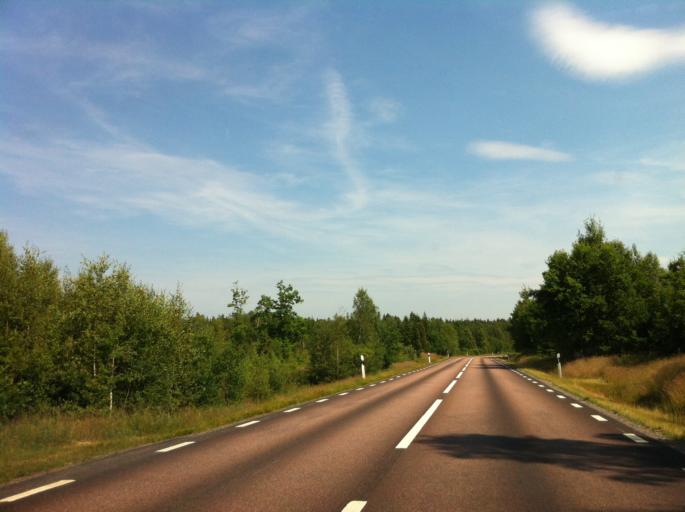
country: SE
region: Kalmar
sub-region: Nybro Kommun
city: Nybro
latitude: 56.8204
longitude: 15.7716
